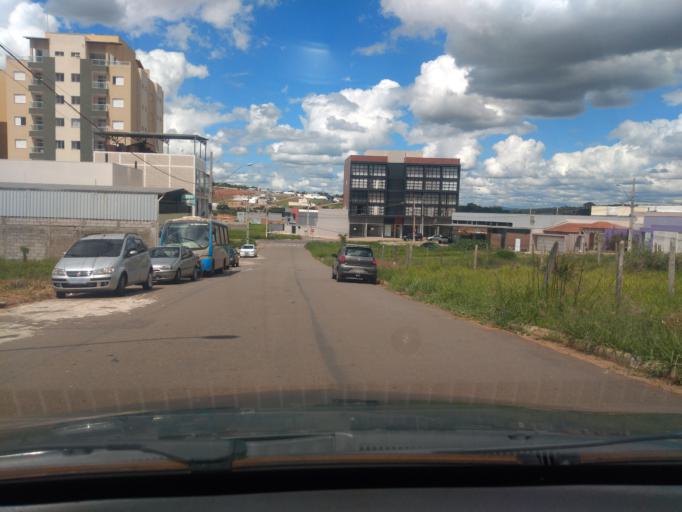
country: BR
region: Minas Gerais
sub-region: Tres Coracoes
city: Tres Coracoes
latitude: -21.6798
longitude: -45.2643
